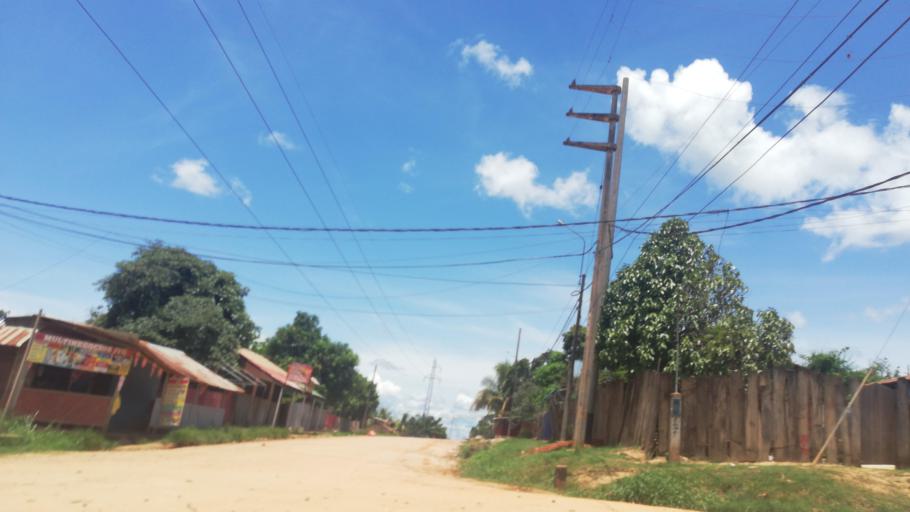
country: PE
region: Ucayali
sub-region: Provincia de Coronel Portillo
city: Puerto Callao
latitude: -8.3589
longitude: -74.5833
